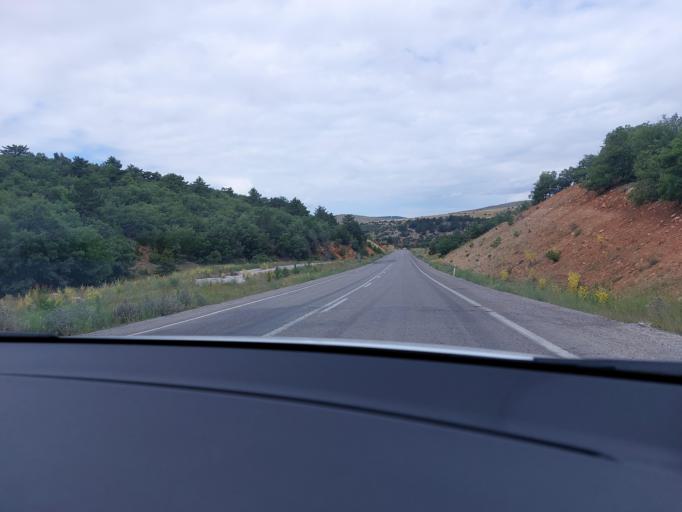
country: TR
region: Konya
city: Doganbey
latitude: 37.8980
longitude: 31.8111
